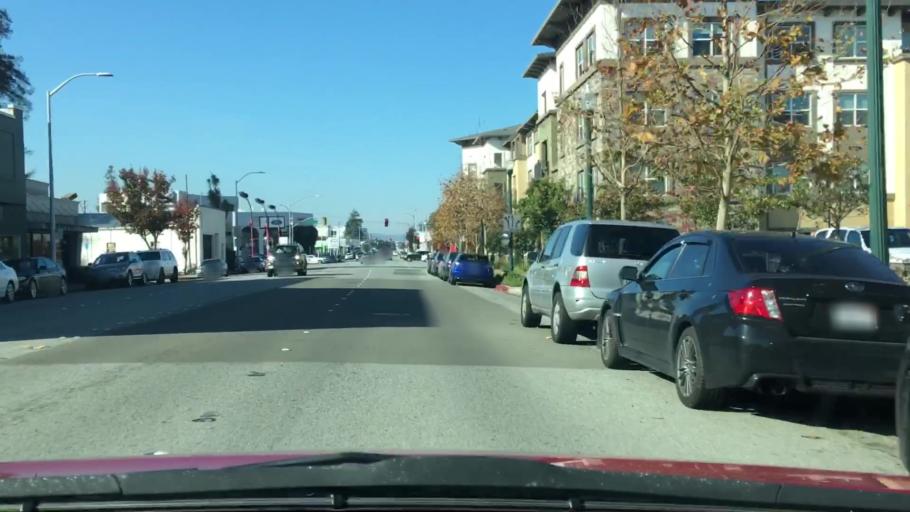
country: US
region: California
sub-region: San Mateo County
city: San Mateo
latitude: 37.5765
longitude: -122.3380
